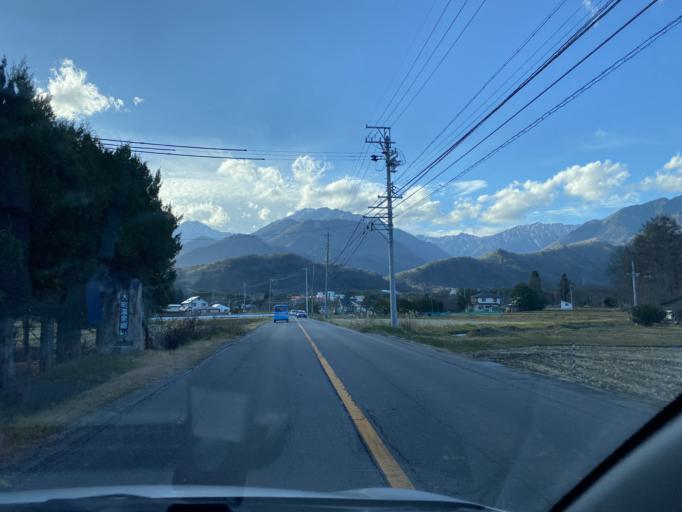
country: JP
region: Nagano
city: Omachi
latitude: 36.5277
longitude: 137.8188
